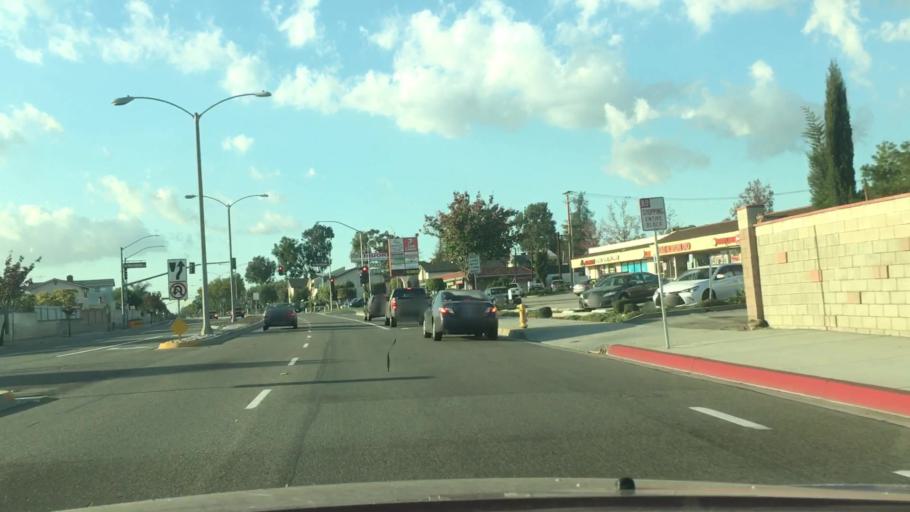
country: US
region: California
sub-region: Orange County
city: Buena Park
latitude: 33.8904
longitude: -118.0011
